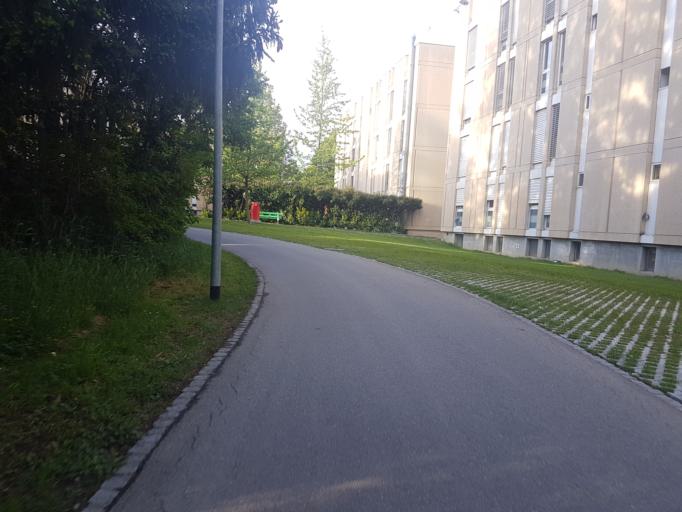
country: CH
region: Geneva
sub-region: Geneva
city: Vernier
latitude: 46.2177
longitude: 6.0947
